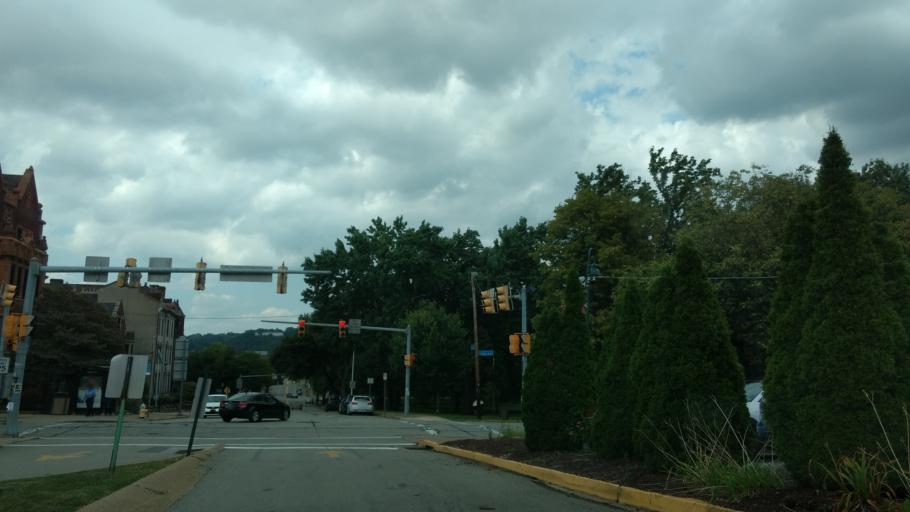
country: US
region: Pennsylvania
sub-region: Allegheny County
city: Pittsburgh
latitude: 40.4503
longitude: -80.0133
